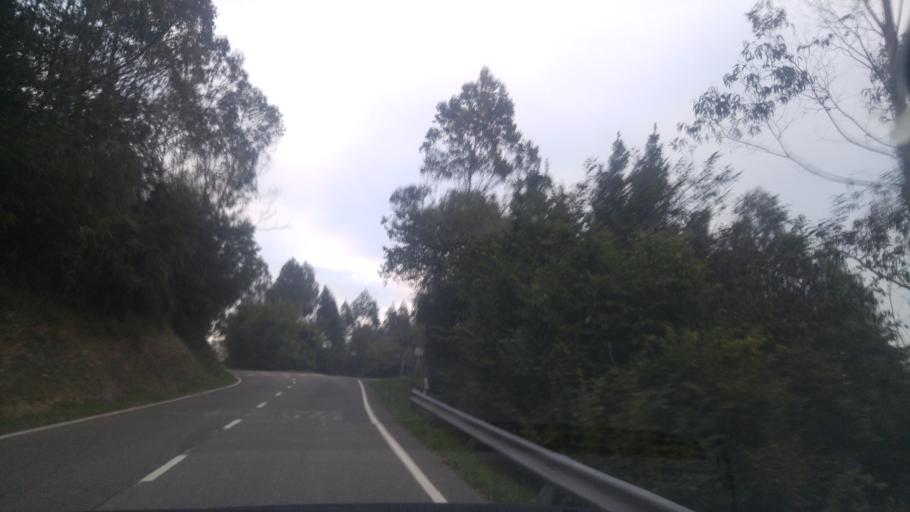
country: ES
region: Asturias
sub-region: Province of Asturias
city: Oviedo
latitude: 43.3856
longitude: -5.8496
